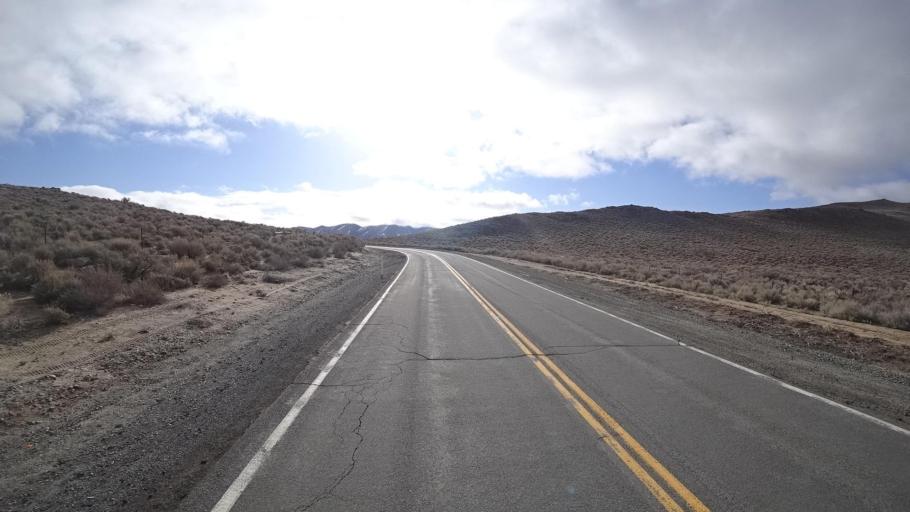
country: US
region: Nevada
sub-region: Washoe County
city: Cold Springs
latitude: 39.8026
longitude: -119.9128
